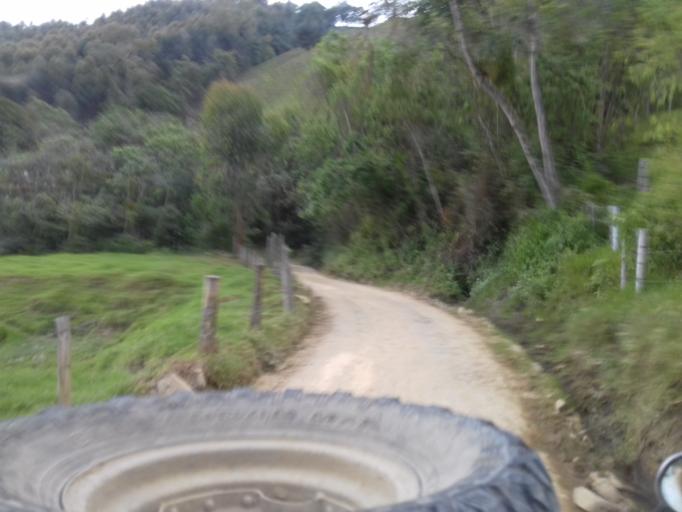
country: CO
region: Quindio
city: Salento
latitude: 4.6279
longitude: -75.5555
